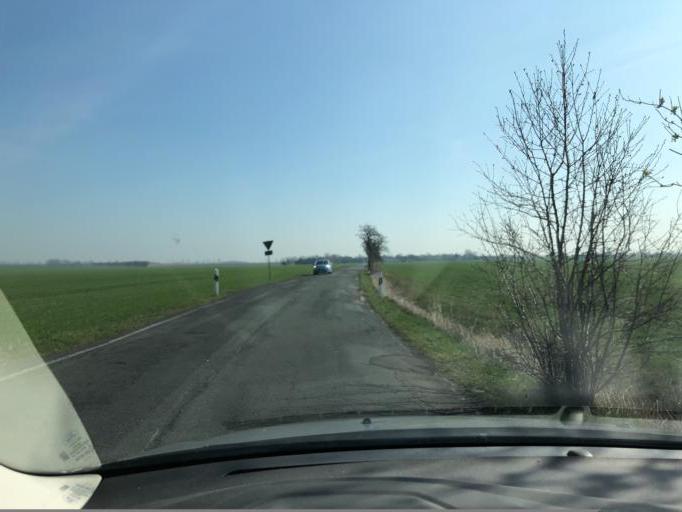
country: DE
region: Saxony
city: Rackwitz
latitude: 51.4251
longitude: 12.4057
